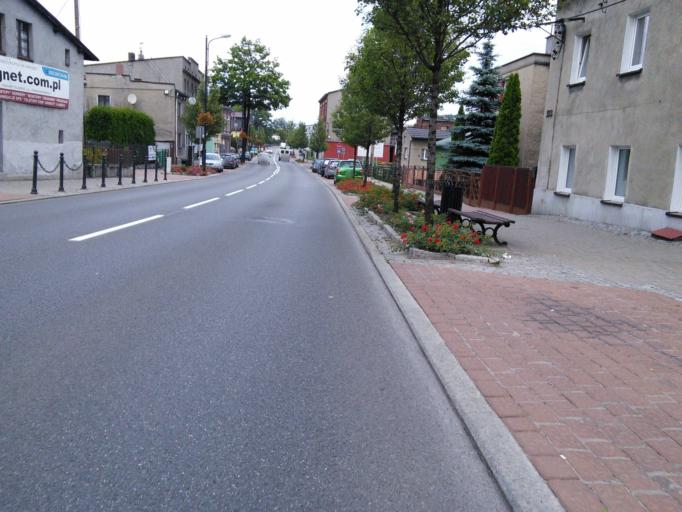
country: PL
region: Silesian Voivodeship
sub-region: Piekary Slaskie
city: Piekary Slaskie
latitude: 50.3870
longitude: 18.9448
